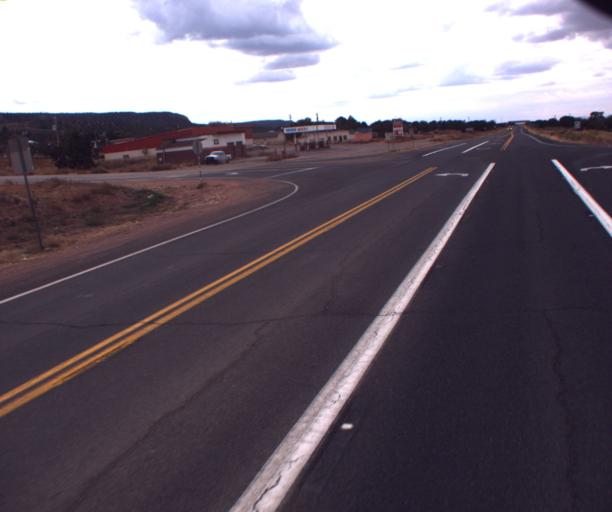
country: US
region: Arizona
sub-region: Navajo County
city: Kayenta
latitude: 36.5616
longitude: -110.5015
